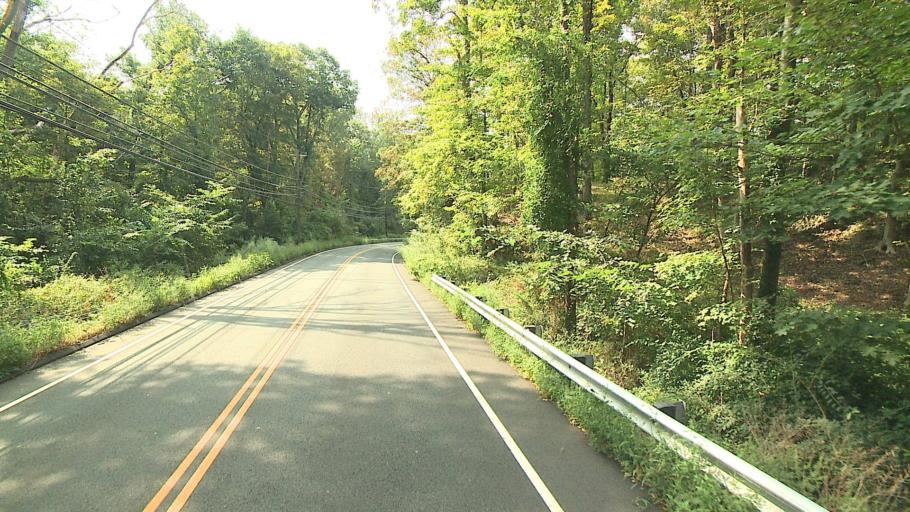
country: US
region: Connecticut
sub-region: Fairfield County
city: Georgetown
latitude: 41.2982
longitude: -73.3887
